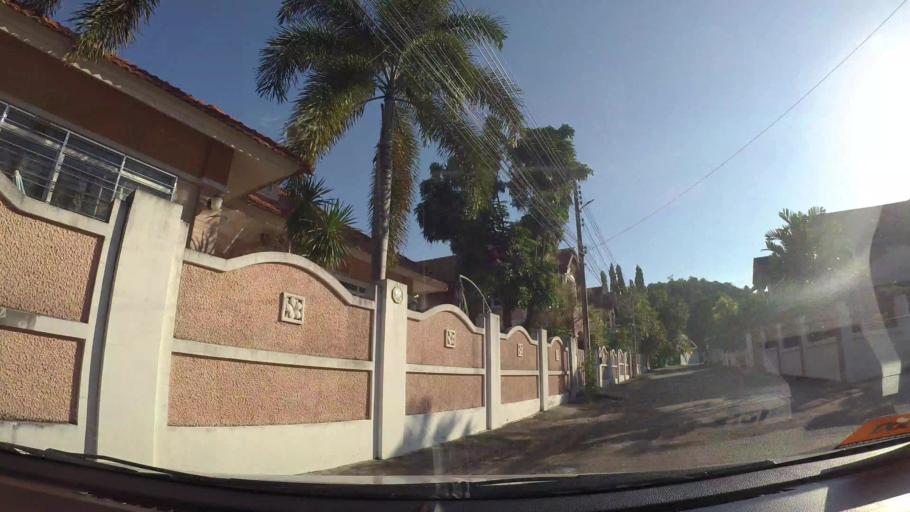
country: TH
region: Chon Buri
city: Si Racha
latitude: 13.1462
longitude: 100.9307
